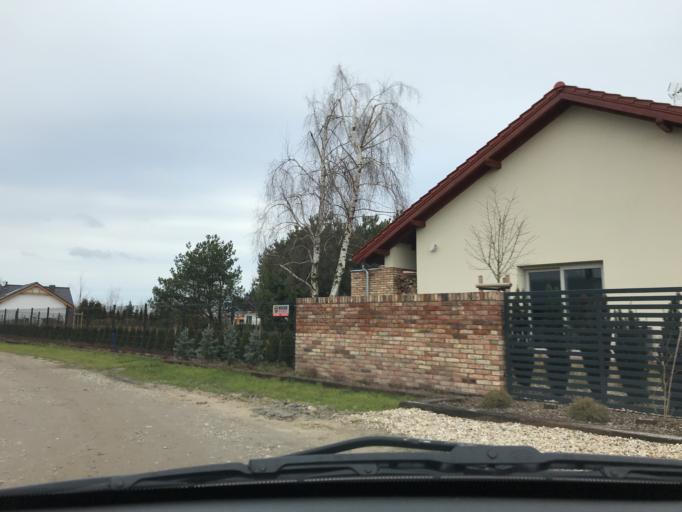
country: PL
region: Greater Poland Voivodeship
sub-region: Powiat poznanski
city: Baranowo
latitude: 52.4002
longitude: 16.7512
